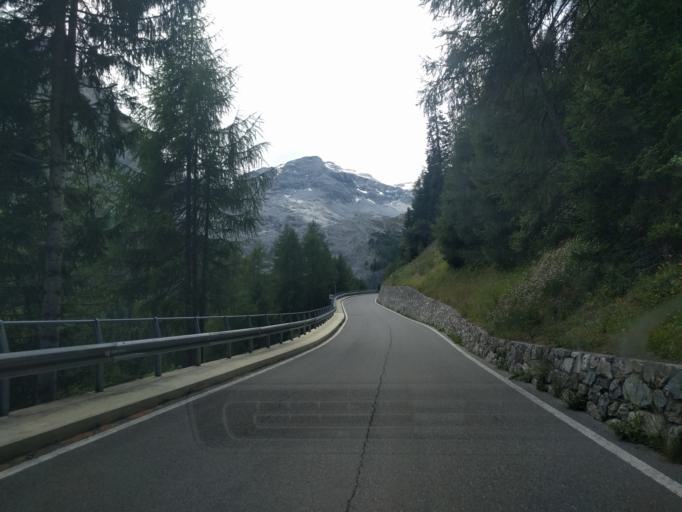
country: IT
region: Trentino-Alto Adige
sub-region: Bolzano
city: Stelvio
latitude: 46.5355
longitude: 10.4971
